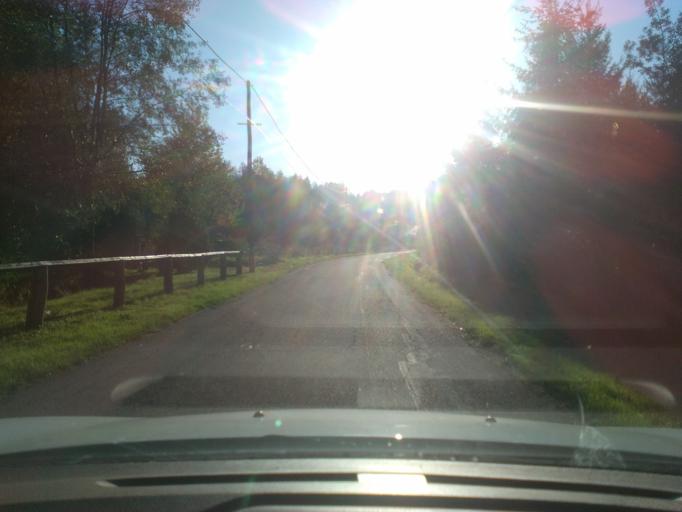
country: FR
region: Lorraine
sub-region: Departement des Vosges
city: Jeanmenil
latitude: 48.2955
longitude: 6.6852
